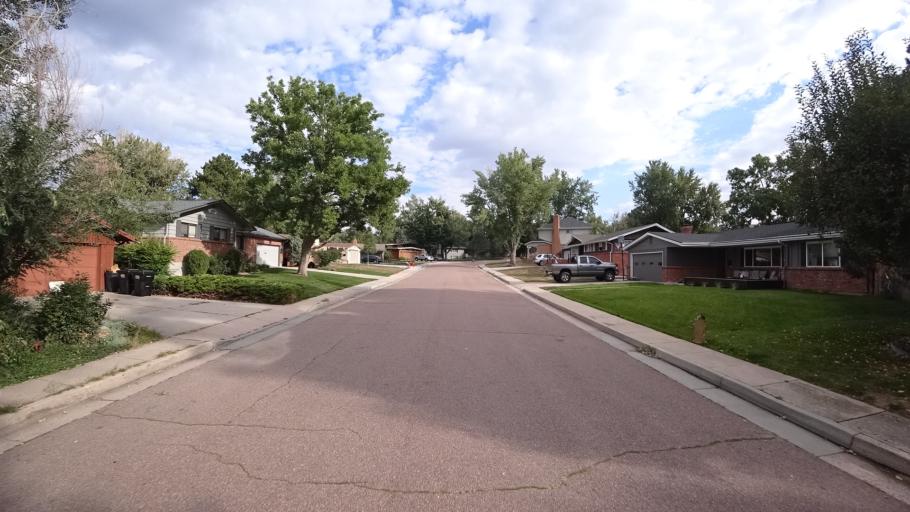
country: US
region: Colorado
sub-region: El Paso County
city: Cimarron Hills
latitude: 38.8624
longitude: -104.7513
